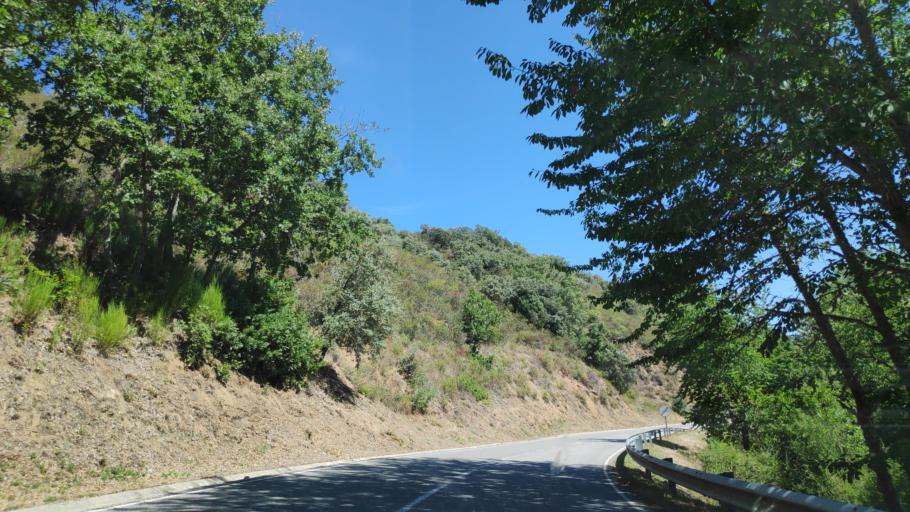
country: PT
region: Braganca
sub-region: Braganca Municipality
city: Braganca
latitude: 41.8920
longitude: -6.7306
